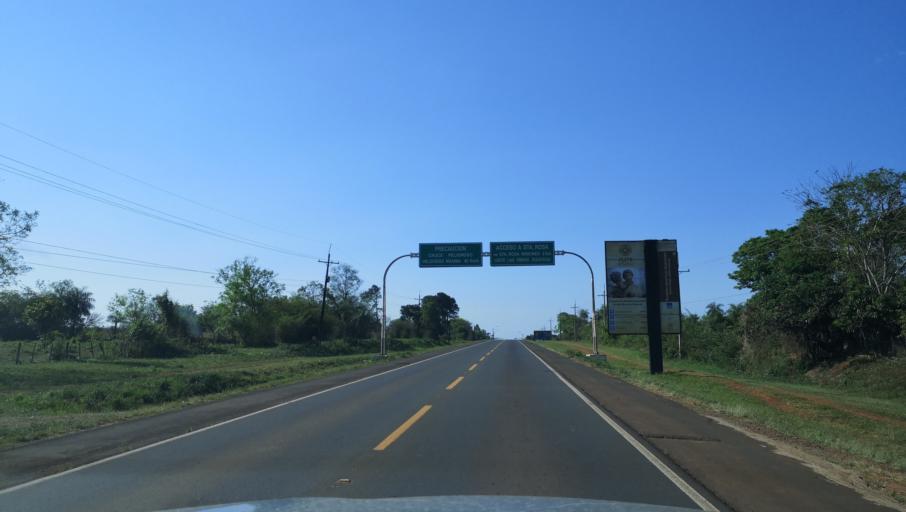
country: PY
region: Misiones
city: Santa Rosa
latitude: -26.9064
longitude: -56.8585
